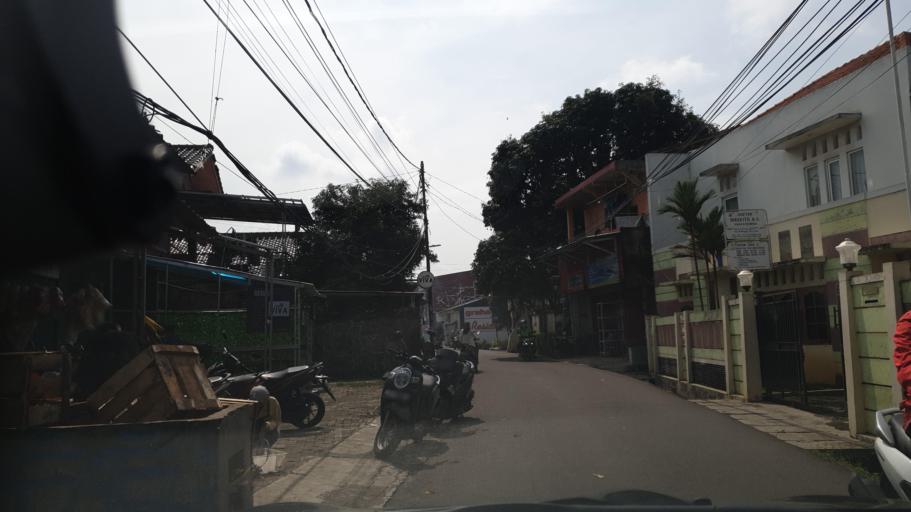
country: ID
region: West Java
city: Pamulang
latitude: -6.3222
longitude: 106.7556
